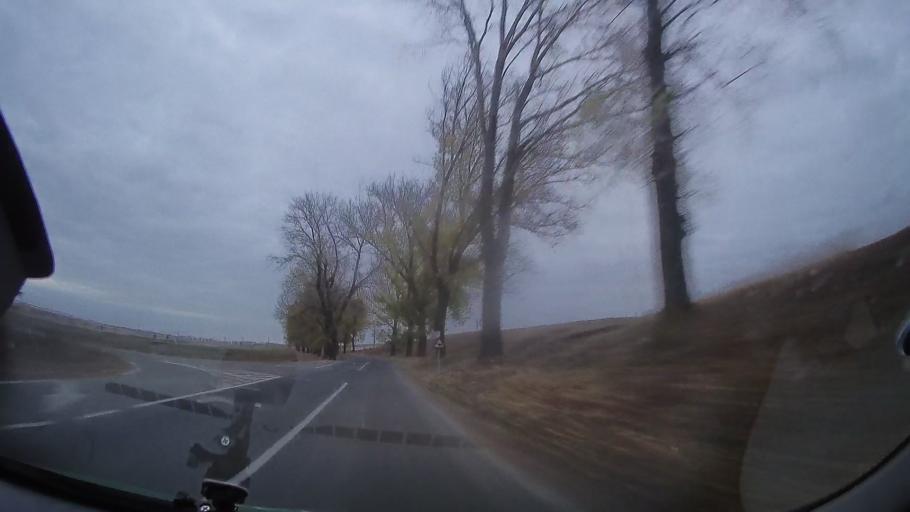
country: RO
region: Tulcea
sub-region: Comuna Mihai Bravu
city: Mihai Bravu
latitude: 44.9612
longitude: 28.6413
